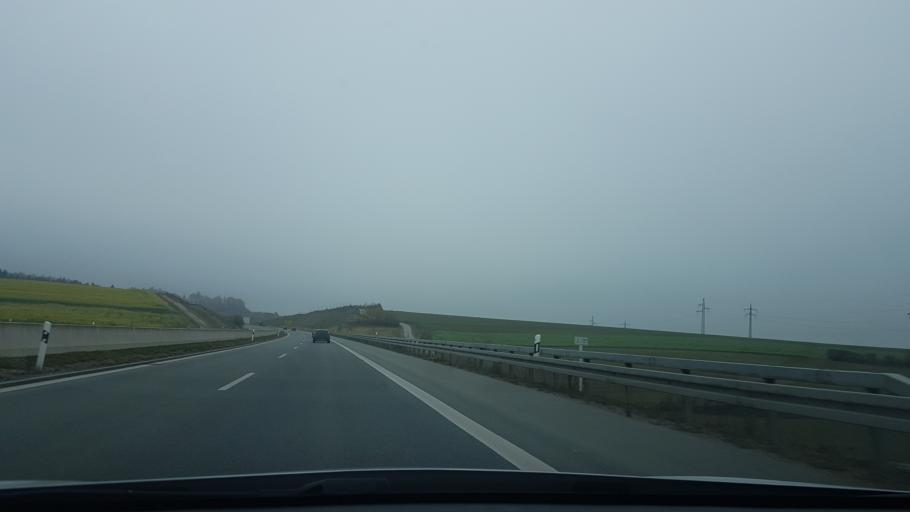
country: DE
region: Bavaria
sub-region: Lower Bavaria
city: Ergoldsbach
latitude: 48.7012
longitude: 12.1785
